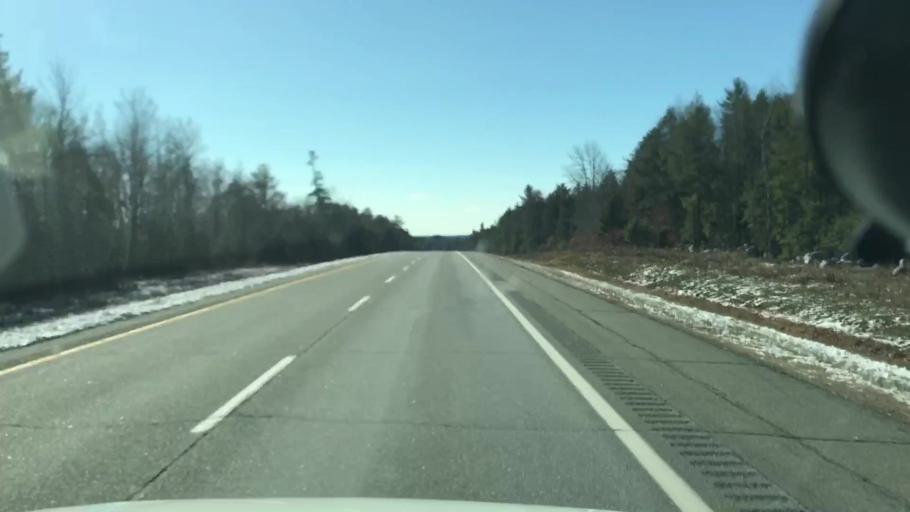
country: US
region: Maine
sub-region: Penobscot County
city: Howland
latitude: 45.2816
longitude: -68.6712
